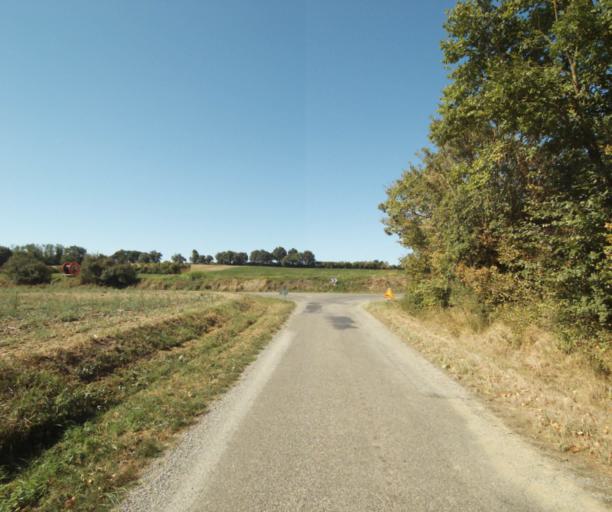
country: FR
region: Midi-Pyrenees
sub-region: Departement du Tarn-et-Garonne
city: Verdun-sur-Garonne
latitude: 43.8386
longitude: 1.2027
